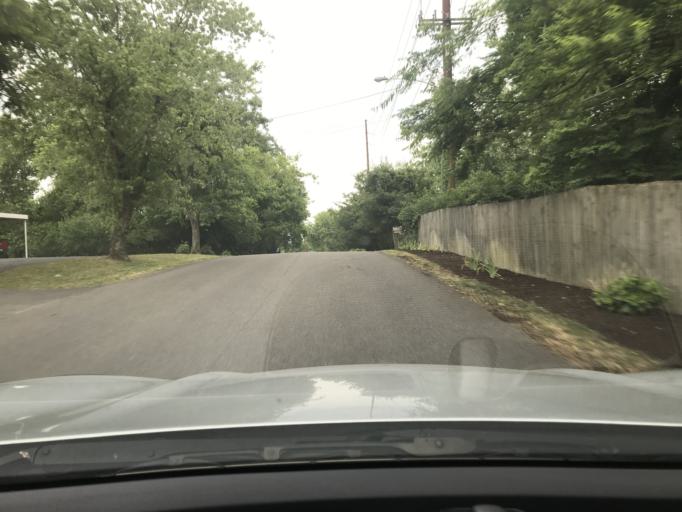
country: US
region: Tennessee
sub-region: Davidson County
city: Goodlettsville
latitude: 36.3069
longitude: -86.7132
